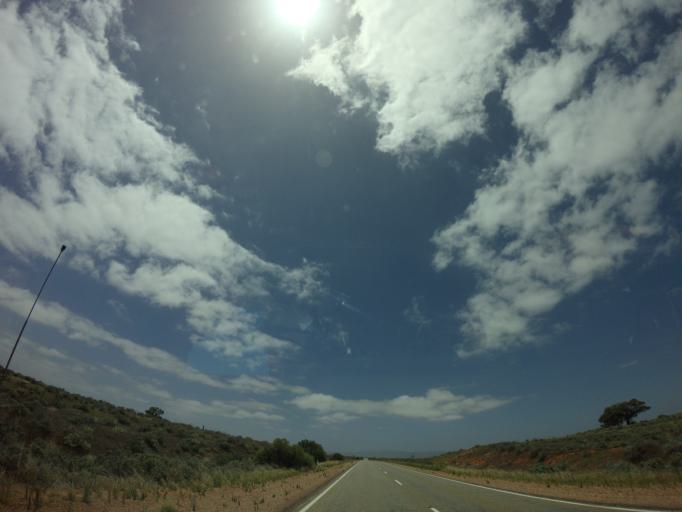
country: AU
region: South Australia
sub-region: Port Augusta
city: Port Augusta West
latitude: -32.4909
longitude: 137.7155
